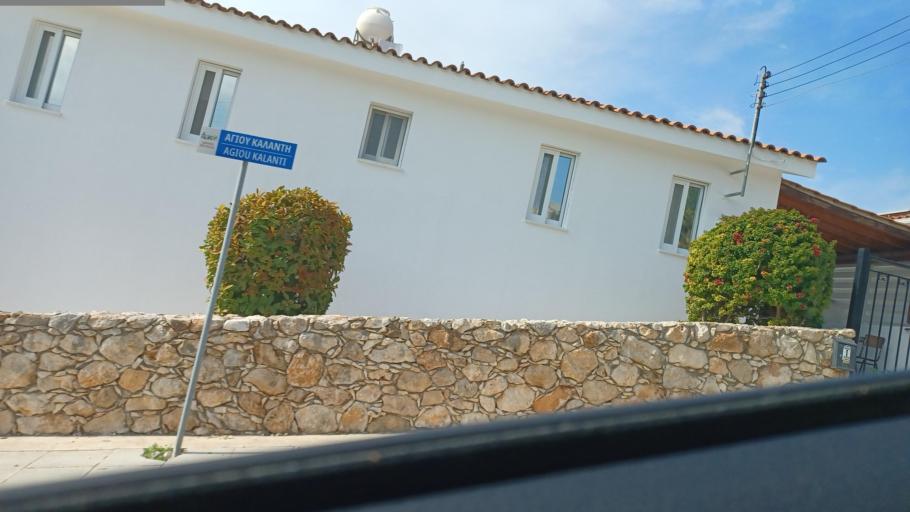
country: CY
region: Pafos
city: Pegeia
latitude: 34.8734
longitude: 32.3722
